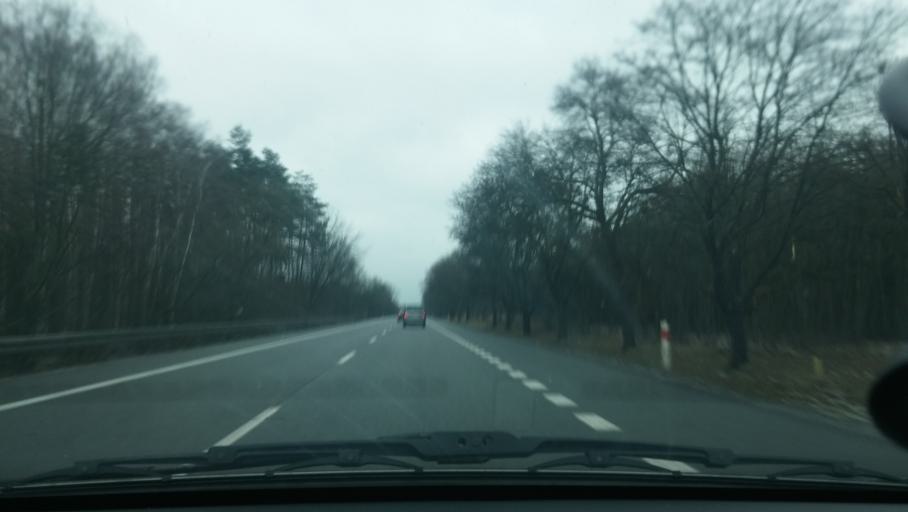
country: PL
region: Masovian Voivodeship
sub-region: Powiat wegrowski
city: Grebkow
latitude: 52.2094
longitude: 21.8874
